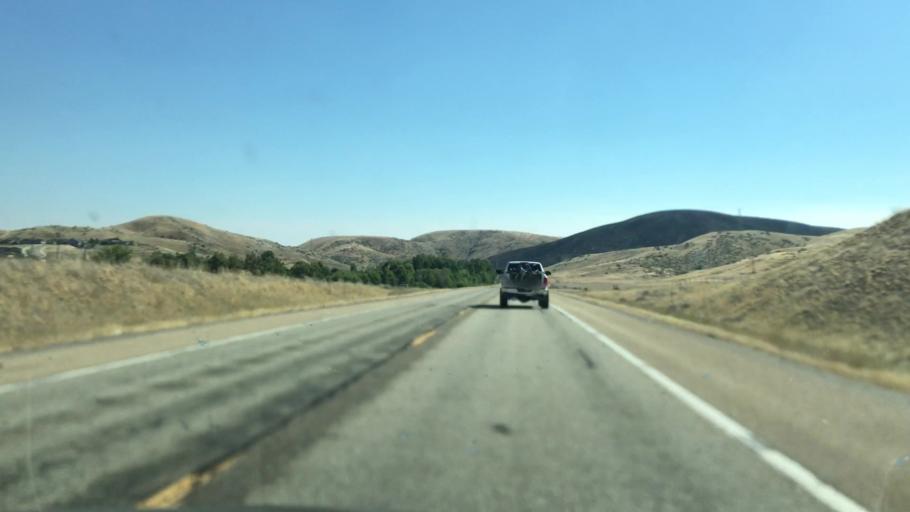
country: US
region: Idaho
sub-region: Ada County
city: Eagle
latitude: 43.7795
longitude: -116.2640
